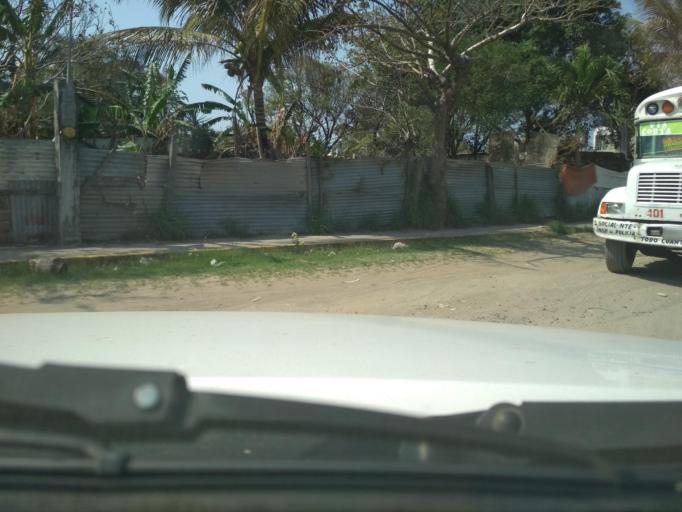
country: MX
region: Veracruz
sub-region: Veracruz
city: Colonia Chalchihuecan
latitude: 19.2122
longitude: -96.2128
